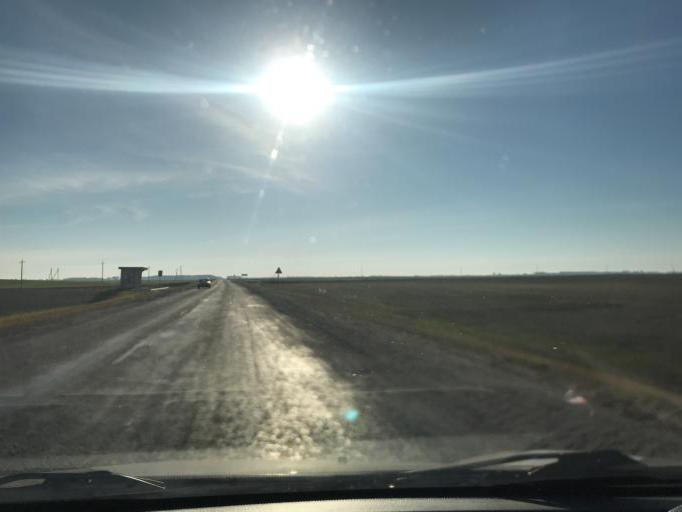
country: BY
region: Gomel
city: Khoyniki
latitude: 51.8363
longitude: 30.0449
